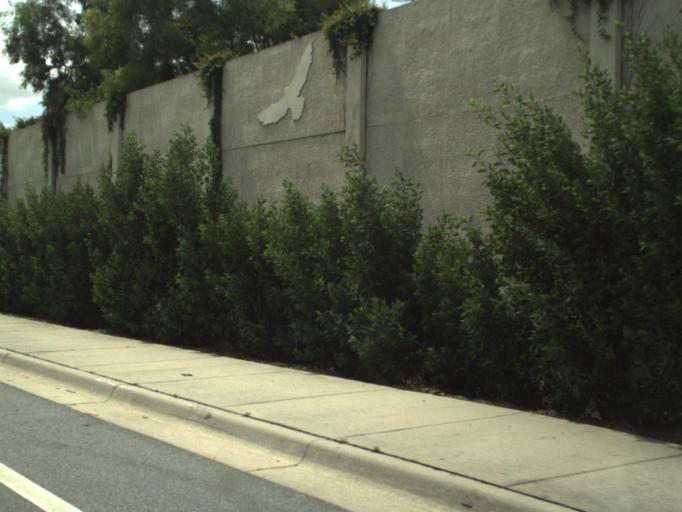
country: US
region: Florida
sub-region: Broward County
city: Pine Island Ridge
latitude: 26.0990
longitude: -80.2536
